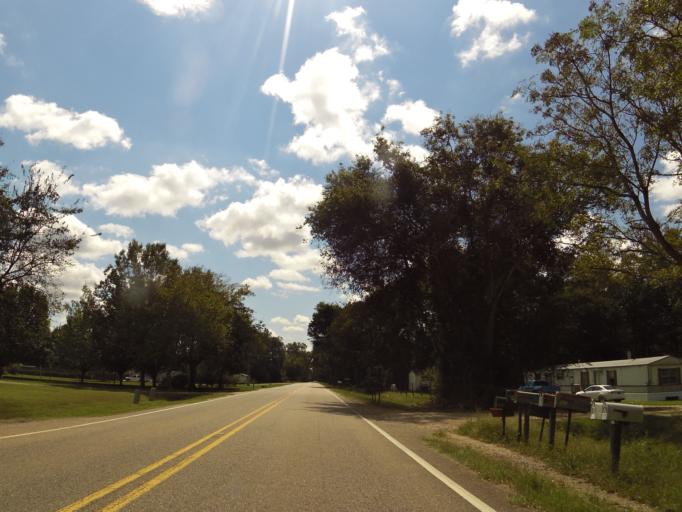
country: US
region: Alabama
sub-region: Dallas County
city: Selma
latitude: 32.4777
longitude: -87.0927
